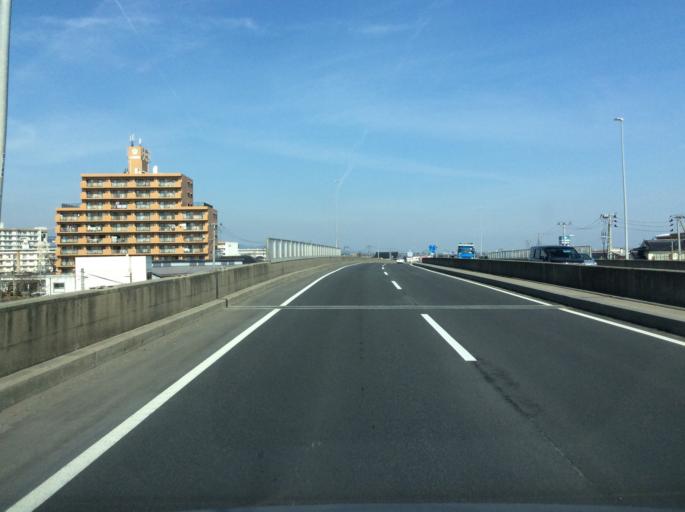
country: JP
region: Fukushima
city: Koriyama
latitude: 37.4073
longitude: 140.3435
